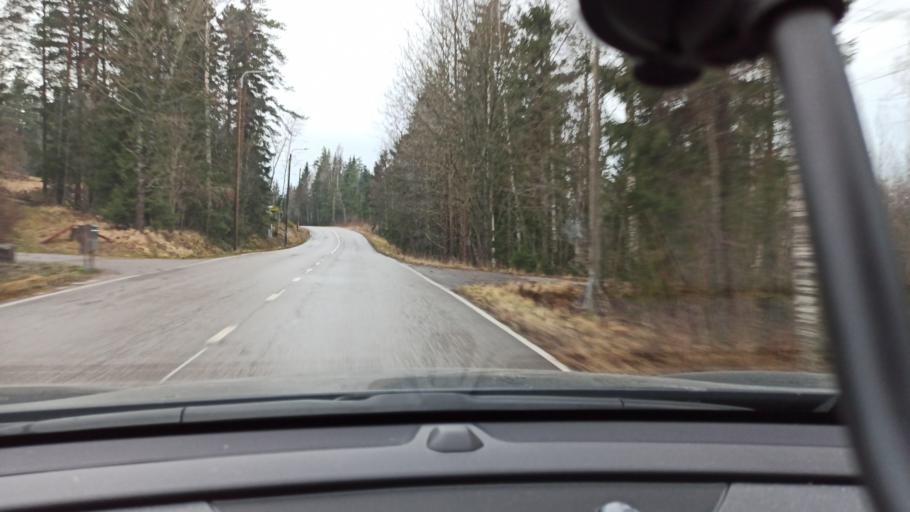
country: FI
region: Uusimaa
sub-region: Helsinki
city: Kirkkonummi
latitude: 60.1570
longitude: 24.5021
